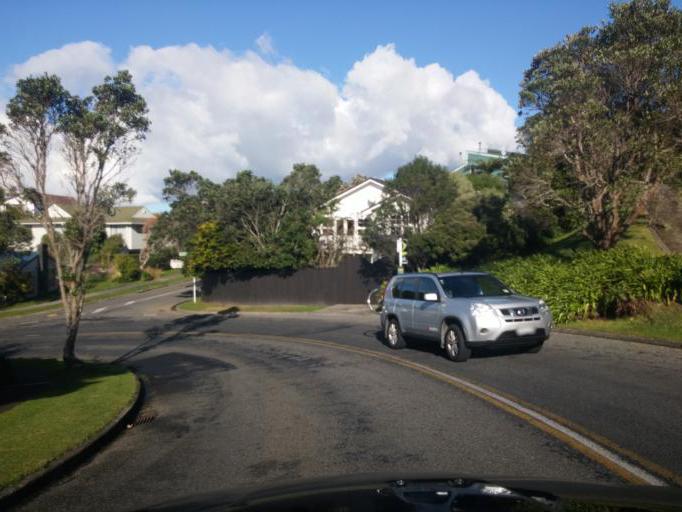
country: NZ
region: Wellington
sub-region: Wellington City
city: Wellington
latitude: -41.2370
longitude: 174.7965
